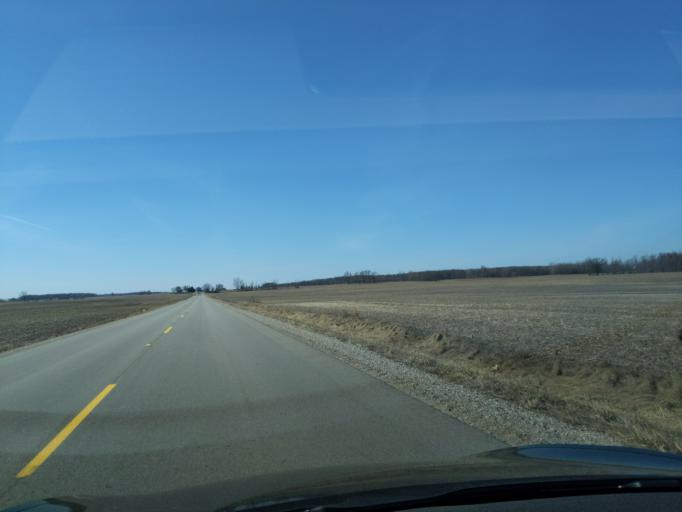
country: US
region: Michigan
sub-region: Eaton County
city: Grand Ledge
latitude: 42.7266
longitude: -84.8656
